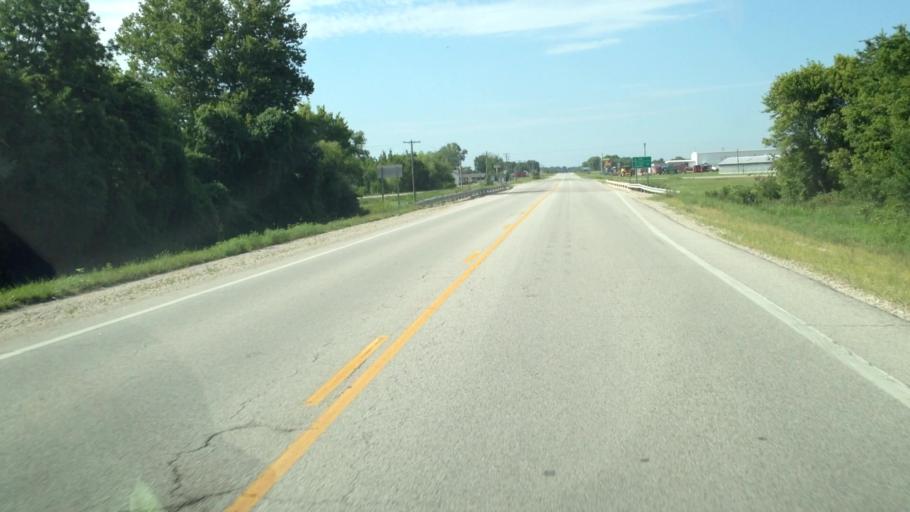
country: US
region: Kansas
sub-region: Neosho County
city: Erie
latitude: 37.5135
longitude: -95.2699
